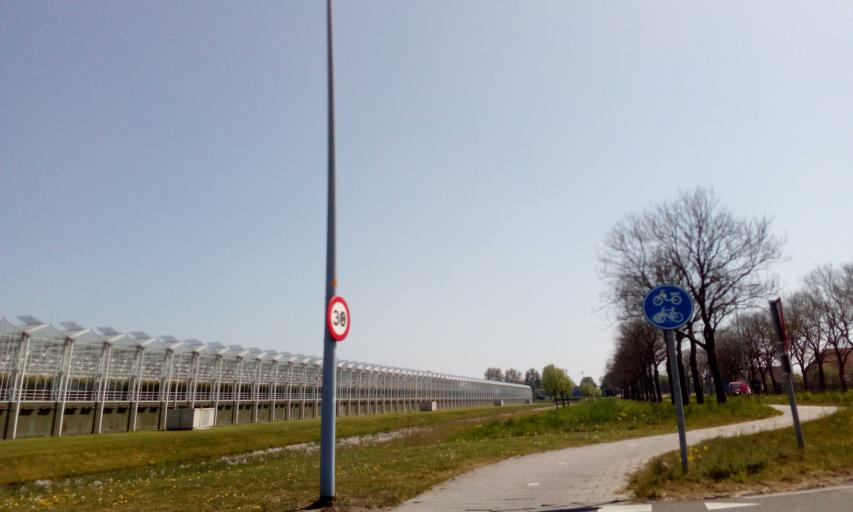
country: NL
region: South Holland
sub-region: Gemeente Kaag en Braassem
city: Leimuiden
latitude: 52.2432
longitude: 4.6745
